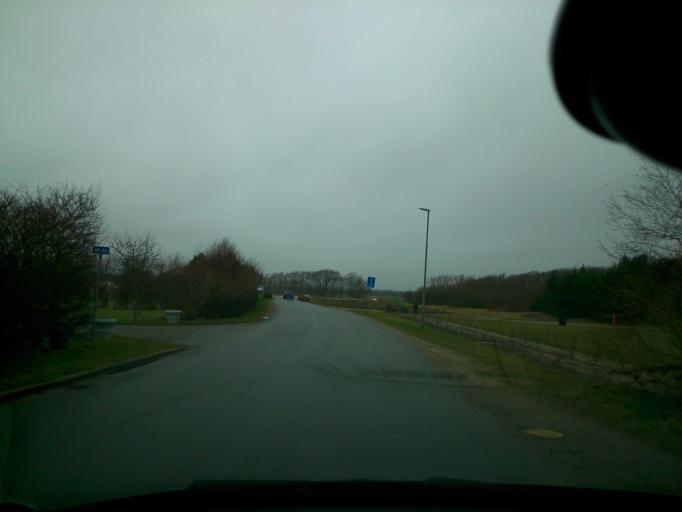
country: DK
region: Central Jutland
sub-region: Ringkobing-Skjern Kommune
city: Ringkobing
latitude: 56.1148
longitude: 8.4218
